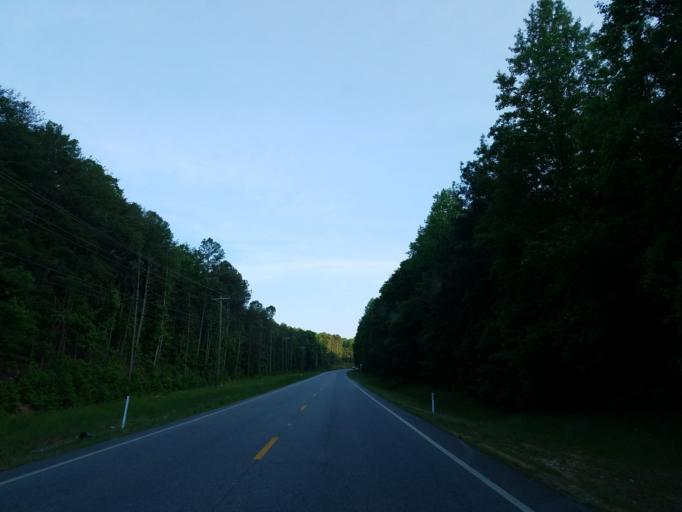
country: US
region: Georgia
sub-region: Whitfield County
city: Dalton
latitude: 34.6688
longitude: -85.0612
